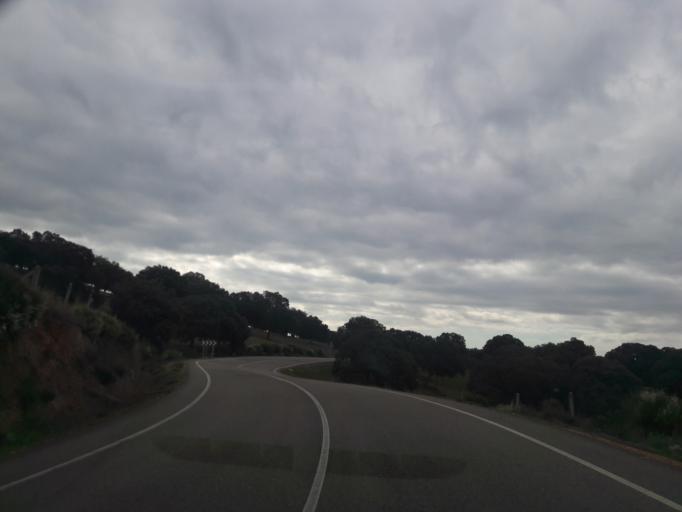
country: ES
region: Castille and Leon
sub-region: Provincia de Salamanca
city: Zamarra
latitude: 40.5383
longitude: -6.4154
